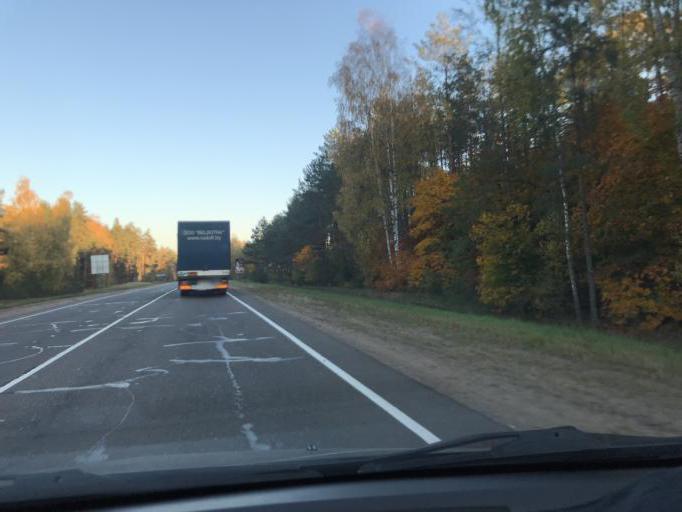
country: BY
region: Minsk
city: Staryya Darohi
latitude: 53.0366
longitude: 28.2137
